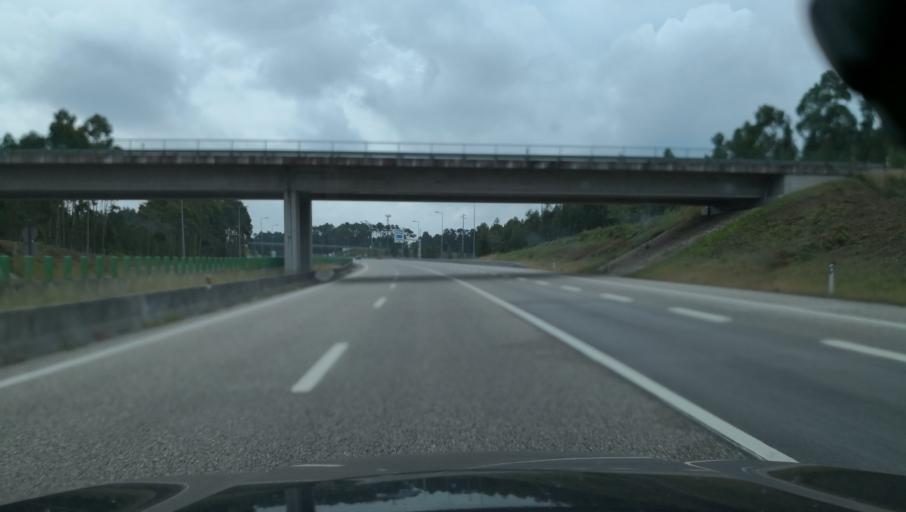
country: PT
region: Leiria
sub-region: Pombal
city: Lourical
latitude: 39.9933
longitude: -8.7978
